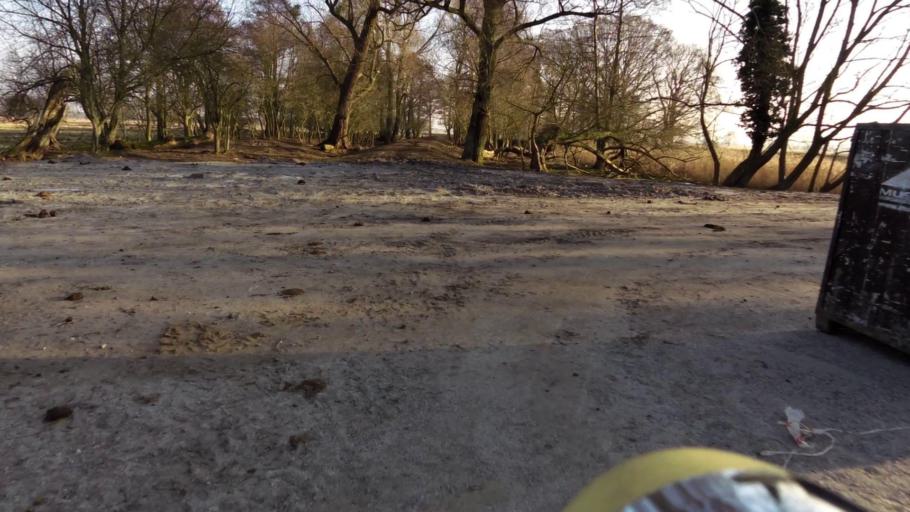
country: PL
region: West Pomeranian Voivodeship
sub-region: Powiat goleniowski
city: Stepnica
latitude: 53.7295
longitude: 14.5583
